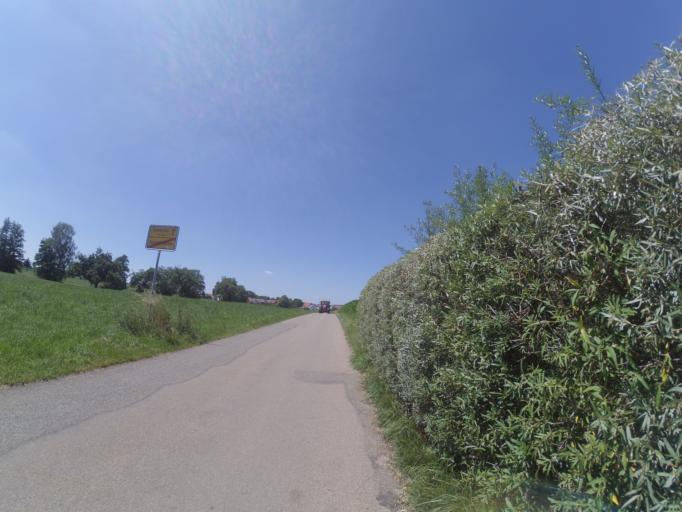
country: DE
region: Baden-Wuerttemberg
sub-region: Tuebingen Region
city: Aulendorf
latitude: 47.9230
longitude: 9.6918
